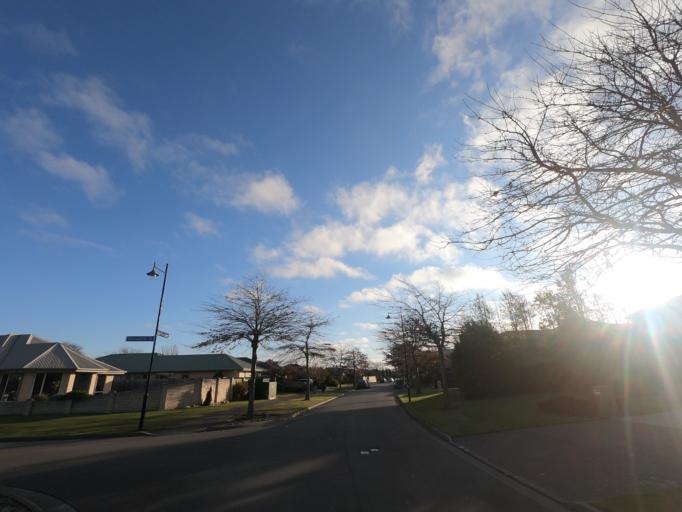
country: NZ
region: Canterbury
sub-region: Selwyn District
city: Prebbleton
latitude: -43.5665
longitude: 172.5702
